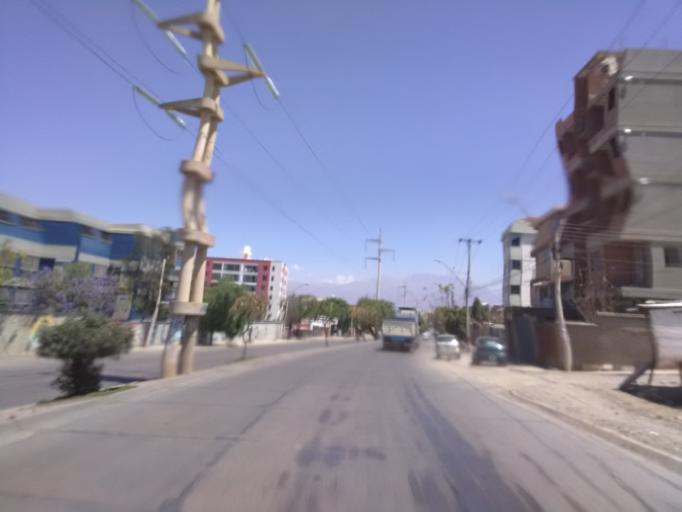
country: BO
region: Cochabamba
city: Cochabamba
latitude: -17.3690
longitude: -66.1440
